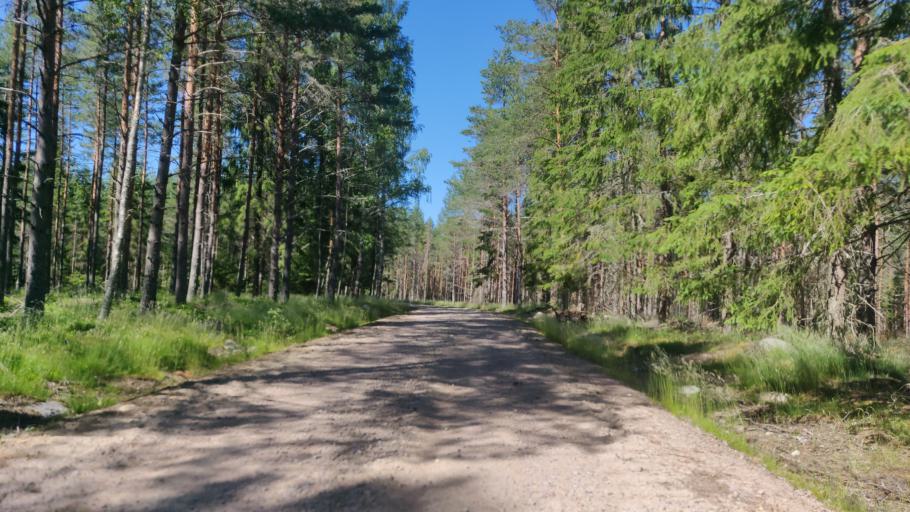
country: SE
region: Vaermland
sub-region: Hagfors Kommun
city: Hagfors
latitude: 59.9767
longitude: 13.6009
